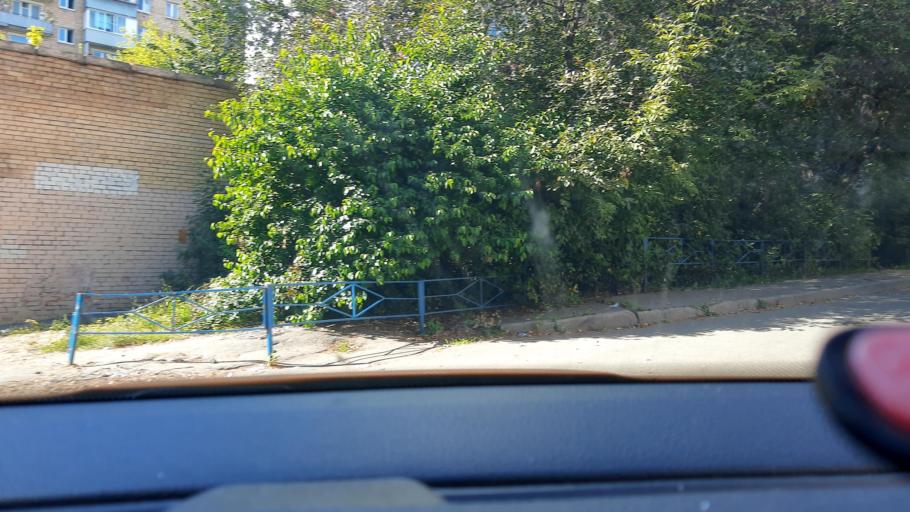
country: RU
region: Moskovskaya
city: Dolgoprudnyy
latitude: 55.9444
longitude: 37.4867
